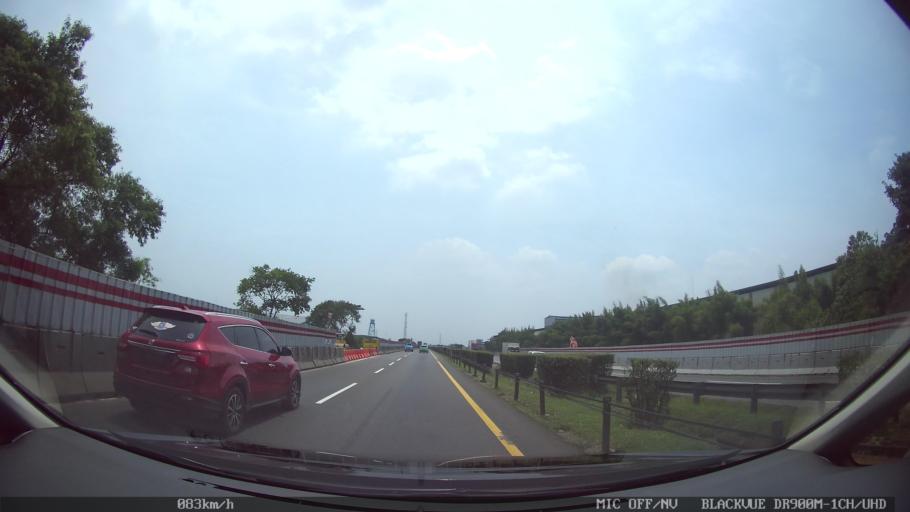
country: ID
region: West Java
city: Kresek
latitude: -6.1676
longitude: 106.3388
